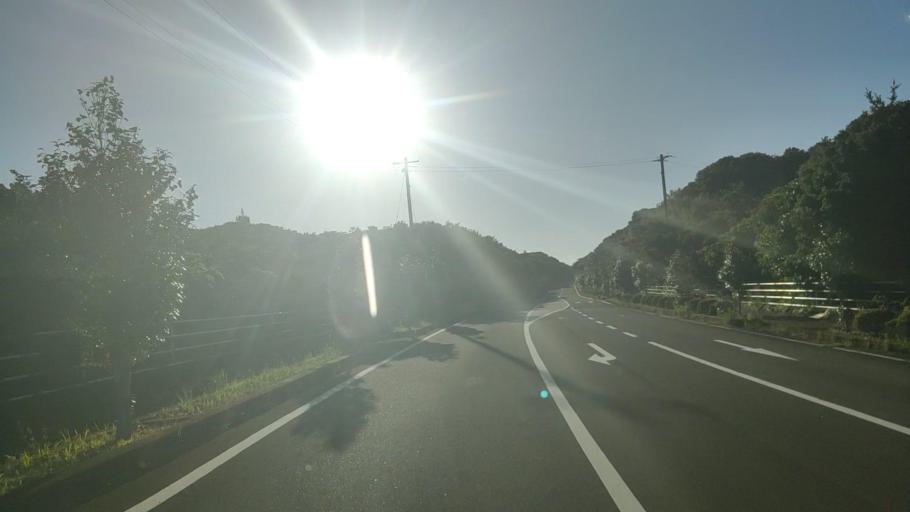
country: JP
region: Mie
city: Toba
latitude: 34.2708
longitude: 136.7836
